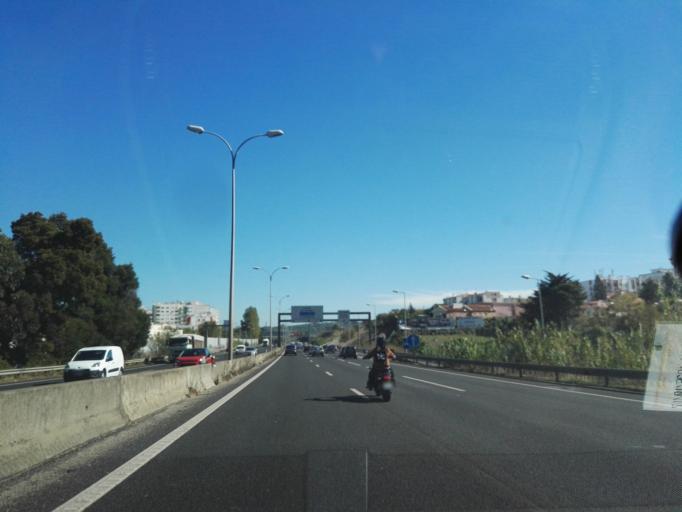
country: PT
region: Lisbon
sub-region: Amadora
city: Amadora
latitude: 38.7416
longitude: -9.2237
